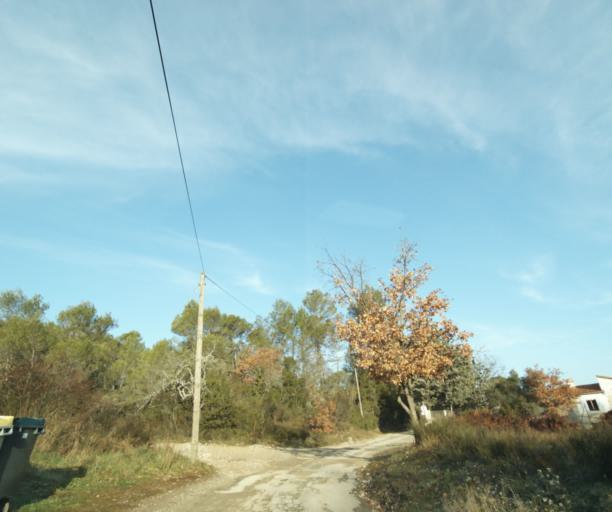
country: FR
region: Provence-Alpes-Cote d'Azur
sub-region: Departement du Var
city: Tourves
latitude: 43.3950
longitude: 5.9342
